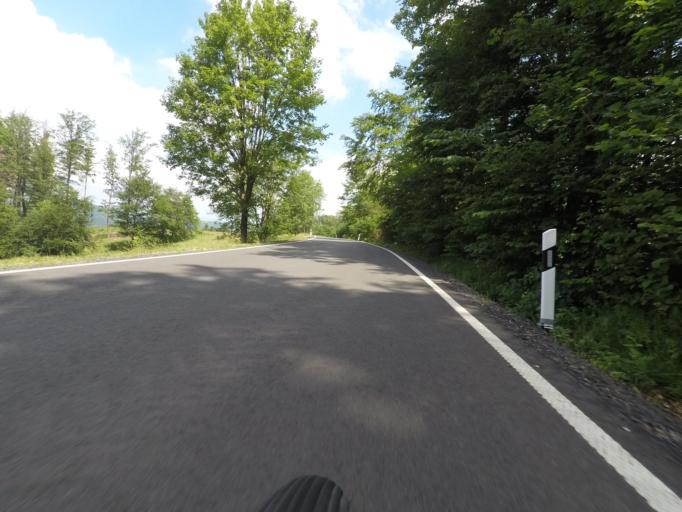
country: DE
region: Hesse
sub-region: Regierungsbezirk Kassel
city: Grossalmerode
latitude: 51.2410
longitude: 9.8695
